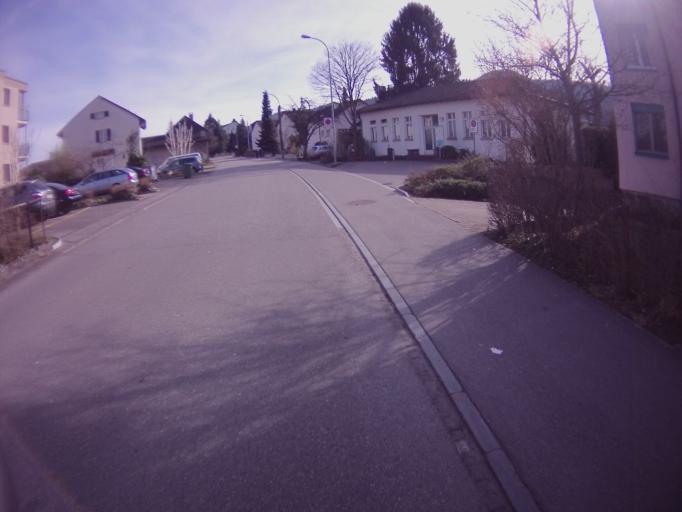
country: CH
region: Aargau
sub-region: Bezirk Baden
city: Neuenhof
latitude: 47.4484
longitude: 8.3320
